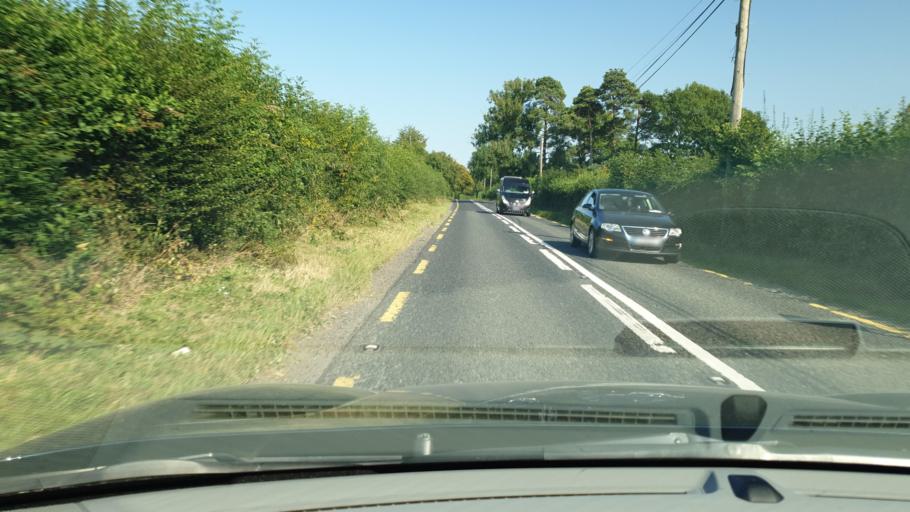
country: IE
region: Leinster
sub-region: An Mhi
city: Newtown Trim
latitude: 53.6291
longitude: -6.7698
